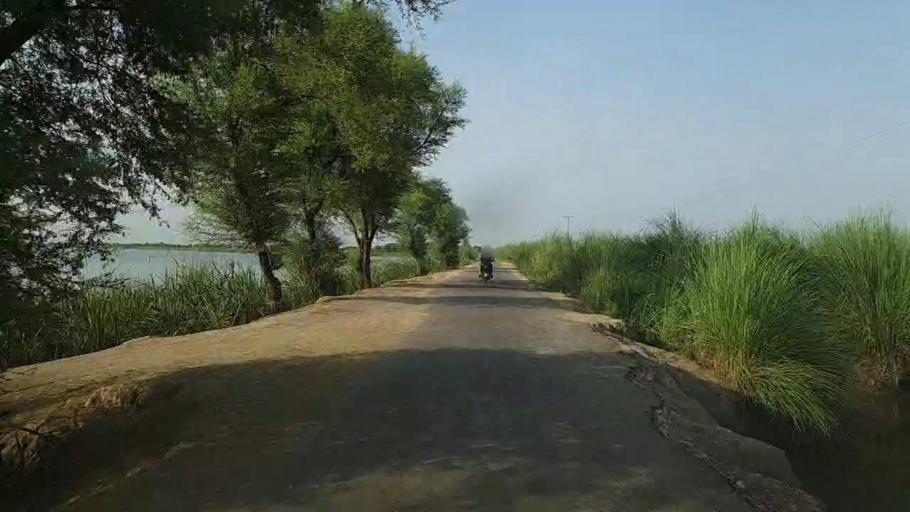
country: PK
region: Sindh
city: Khairpur
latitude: 28.0792
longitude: 69.8134
